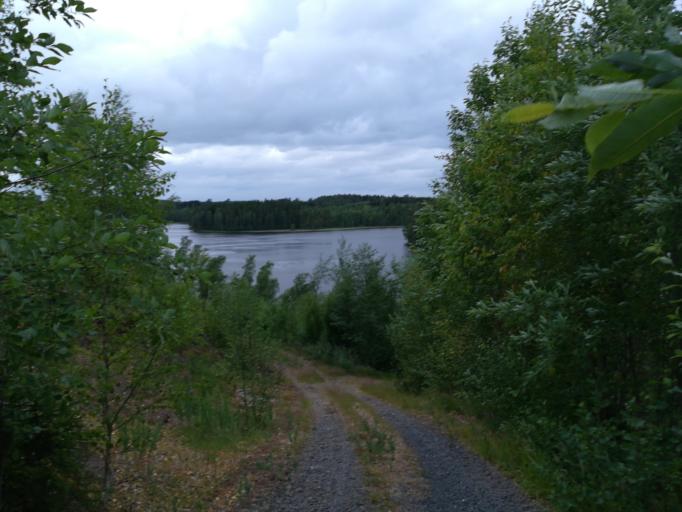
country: FI
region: South Karelia
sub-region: Lappeenranta
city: Savitaipale
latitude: 61.1847
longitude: 27.5565
